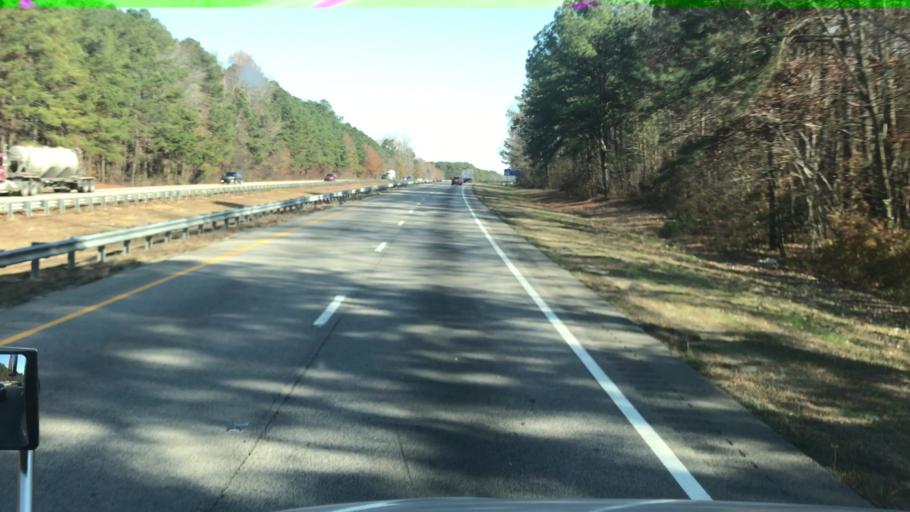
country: US
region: North Carolina
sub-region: Wake County
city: Wendell
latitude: 35.8225
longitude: -78.3849
